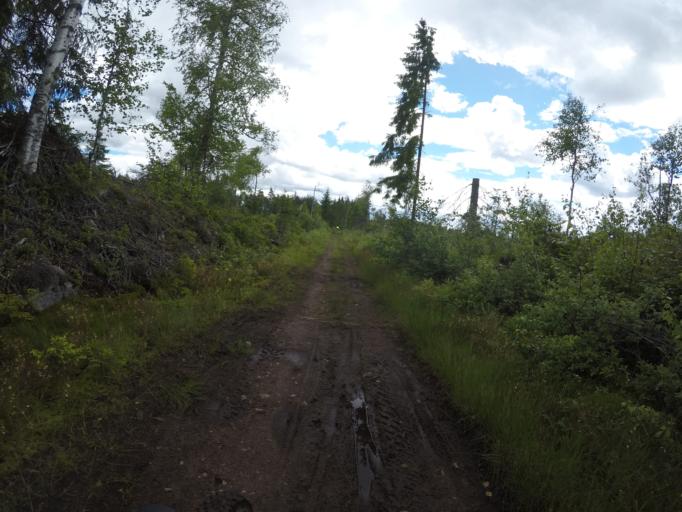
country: SE
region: Vaermland
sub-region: Filipstads Kommun
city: Lesjofors
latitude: 60.1422
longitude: 14.2491
